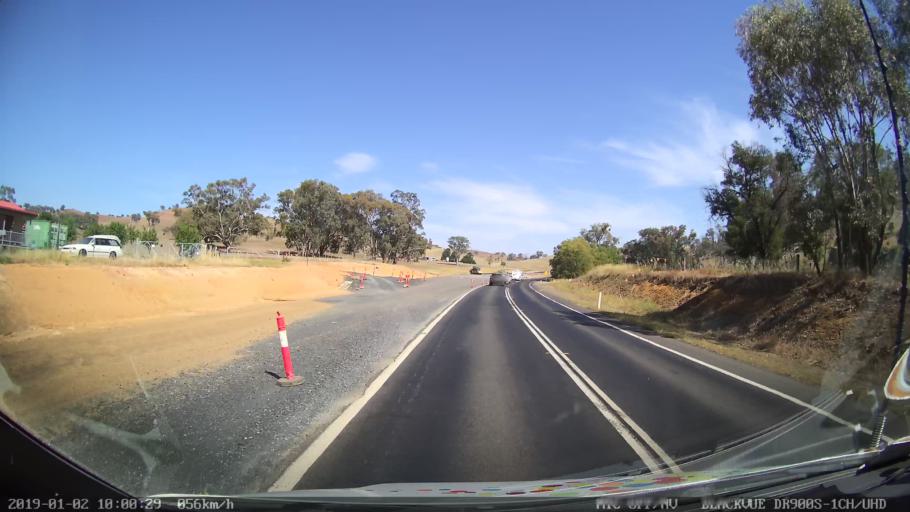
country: AU
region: New South Wales
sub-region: Gundagai
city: Gundagai
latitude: -35.1948
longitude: 148.1315
